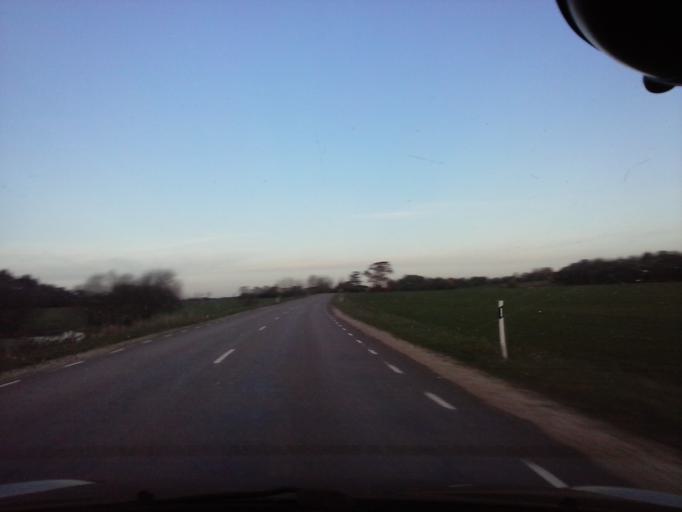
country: EE
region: Harju
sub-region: Nissi vald
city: Turba
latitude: 58.9067
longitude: 24.1220
